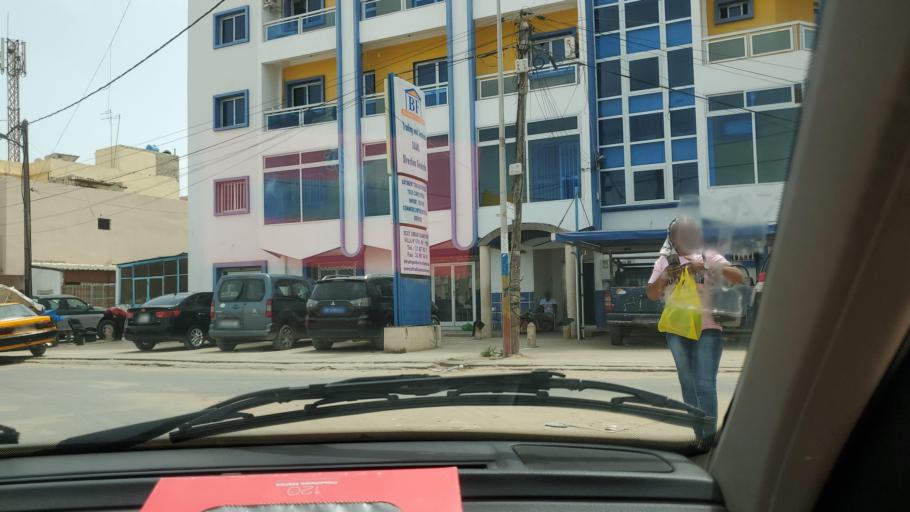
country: SN
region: Dakar
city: Grand Dakar
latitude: 14.7398
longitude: -17.4581
